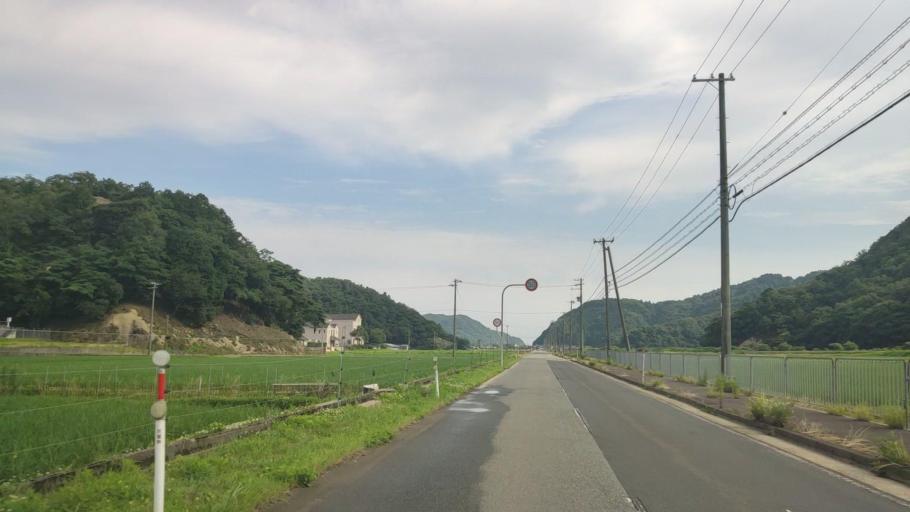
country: JP
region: Hyogo
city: Toyooka
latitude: 35.6239
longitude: 134.8412
